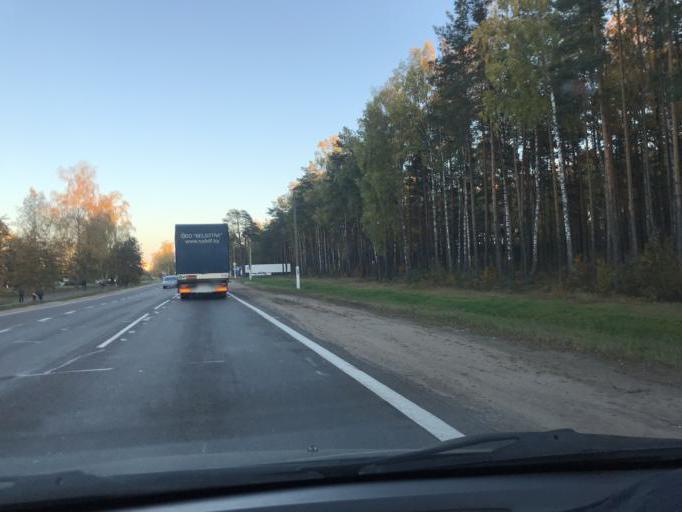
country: BY
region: Minsk
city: Staryya Darohi
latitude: 53.0334
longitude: 28.2486
